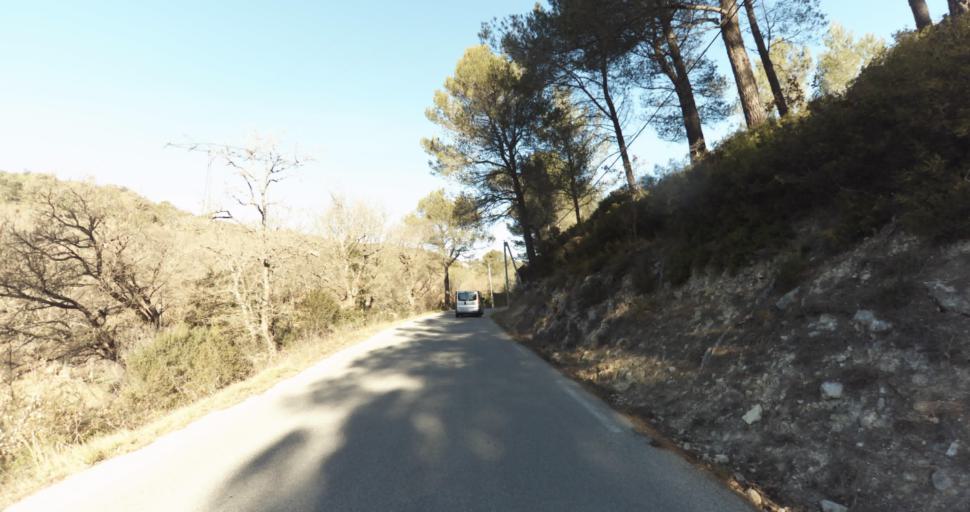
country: FR
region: Provence-Alpes-Cote d'Azur
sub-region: Departement des Bouches-du-Rhone
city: Peypin
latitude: 43.3667
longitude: 5.5650
